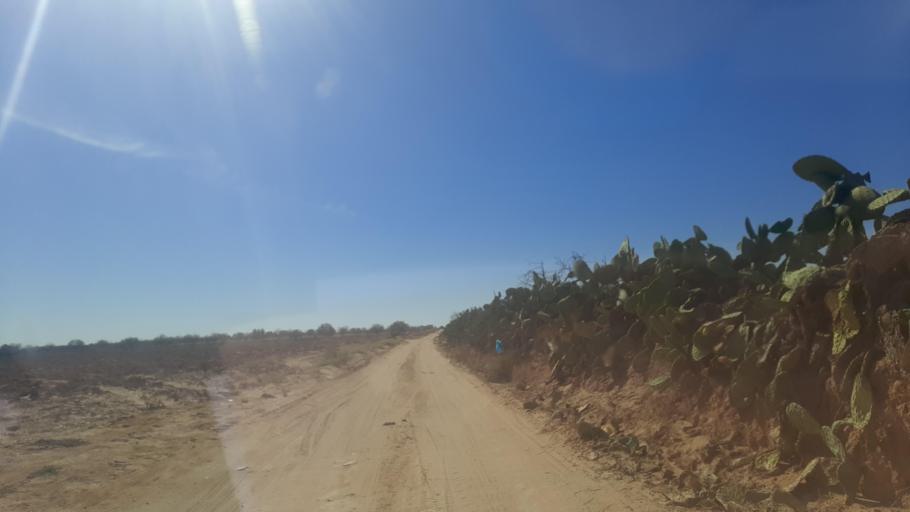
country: TN
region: Safaqis
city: Sfax
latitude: 34.8531
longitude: 10.5626
